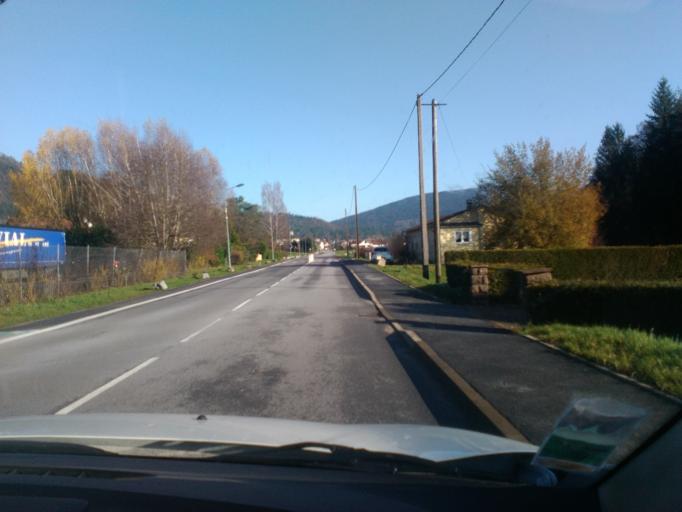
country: FR
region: Lorraine
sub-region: Departement des Vosges
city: Saint-Ame
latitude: 48.0179
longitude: 6.6535
